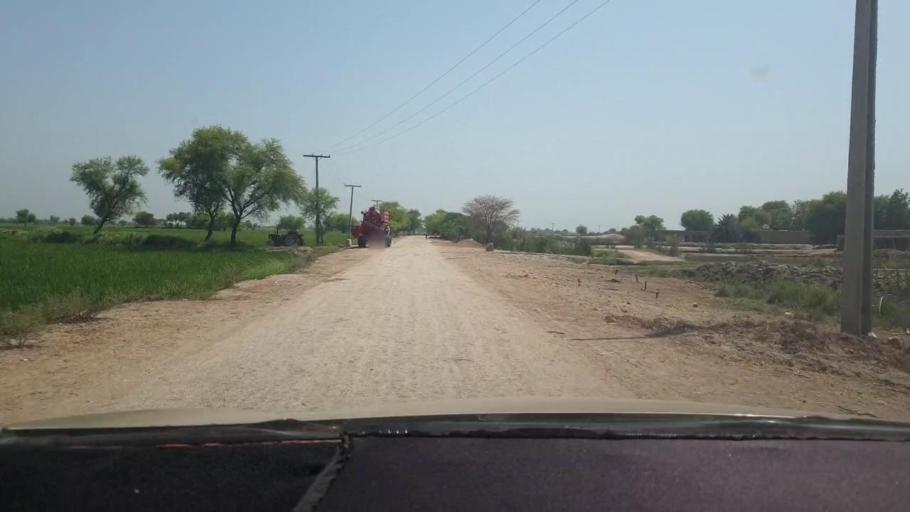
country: PK
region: Sindh
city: Miro Khan
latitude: 27.6820
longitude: 68.0953
